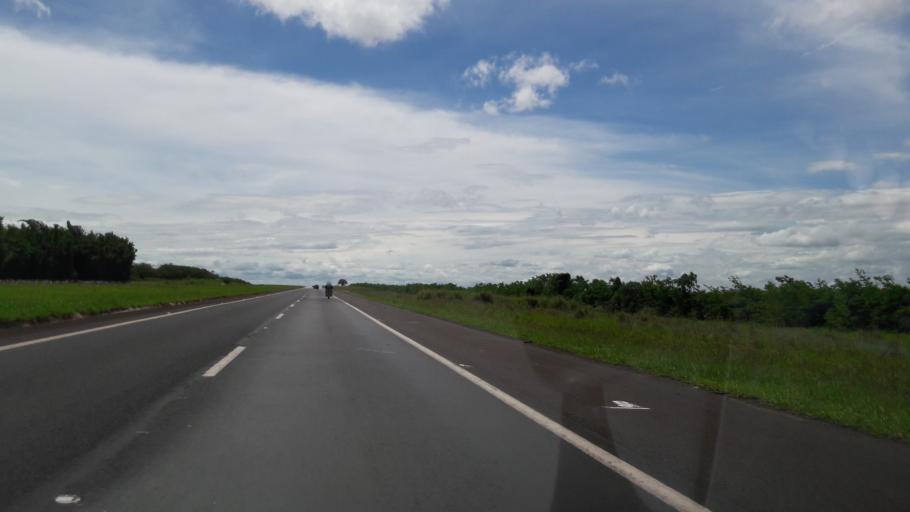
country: BR
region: Sao Paulo
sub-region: Avare
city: Avare
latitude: -22.9476
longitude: -48.8886
